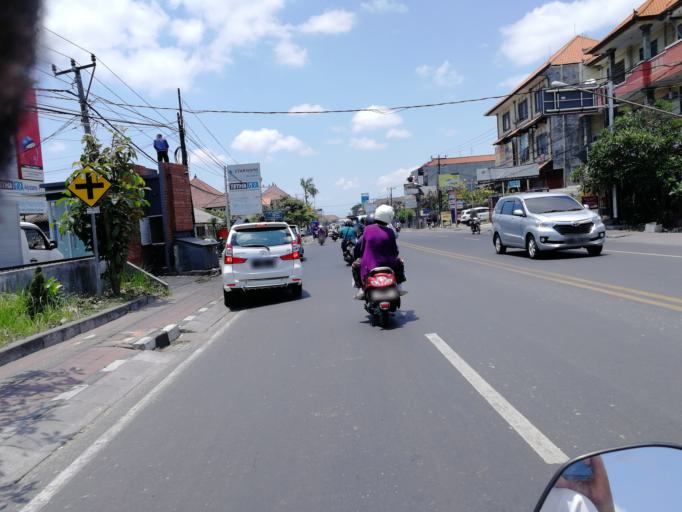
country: ID
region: Bali
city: Banjar Kertasari
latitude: -8.6381
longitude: 115.1966
